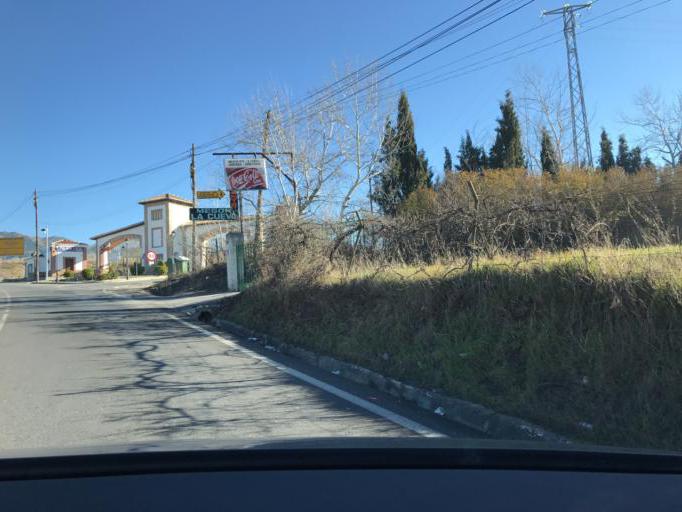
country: ES
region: Andalusia
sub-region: Provincia de Granada
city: Jun
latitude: 37.2190
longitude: -3.5871
